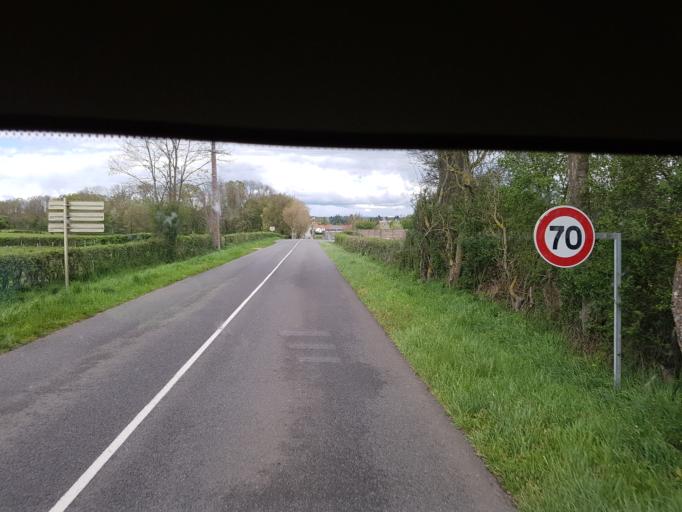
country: FR
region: Bourgogne
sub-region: Departement de Saone-et-Loire
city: Genelard
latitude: 46.5703
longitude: 4.2354
